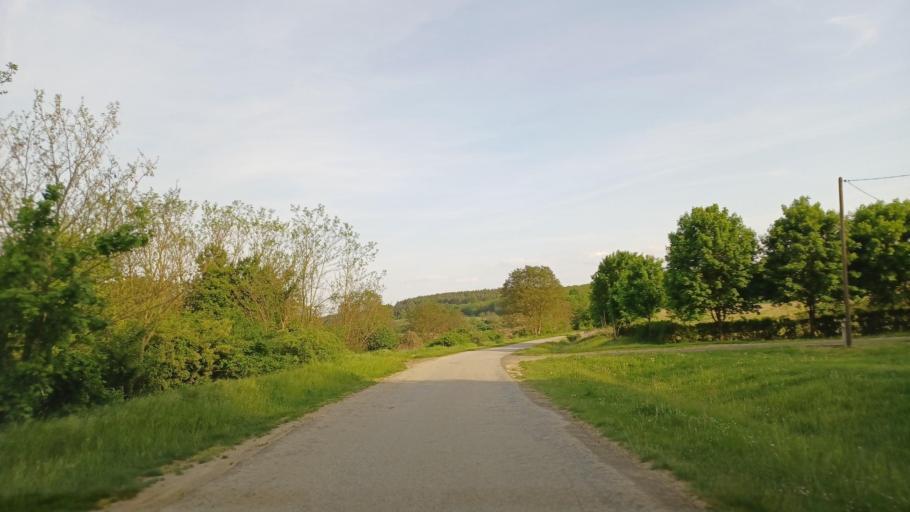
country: HU
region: Baranya
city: Kozarmisleny
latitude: 45.9678
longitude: 18.3655
